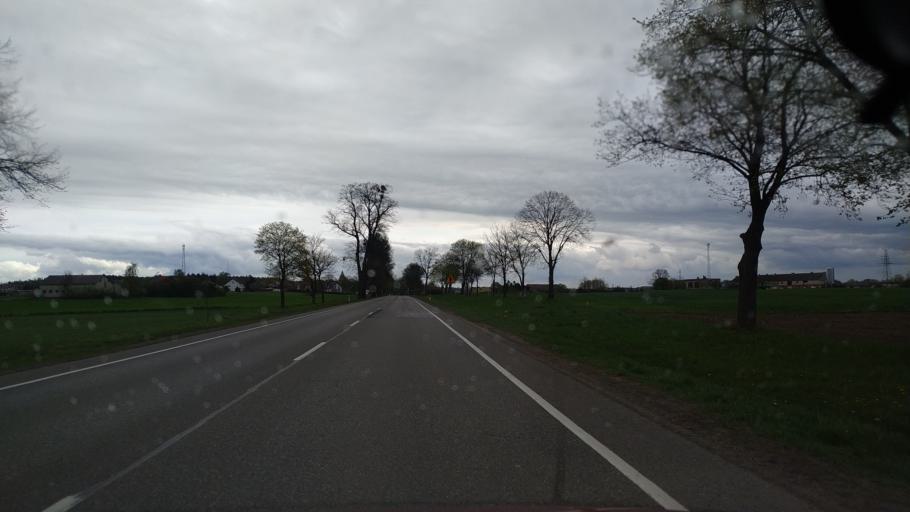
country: PL
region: Pomeranian Voivodeship
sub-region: Powiat starogardzki
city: Lubichowo
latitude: 53.9352
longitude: 18.4264
